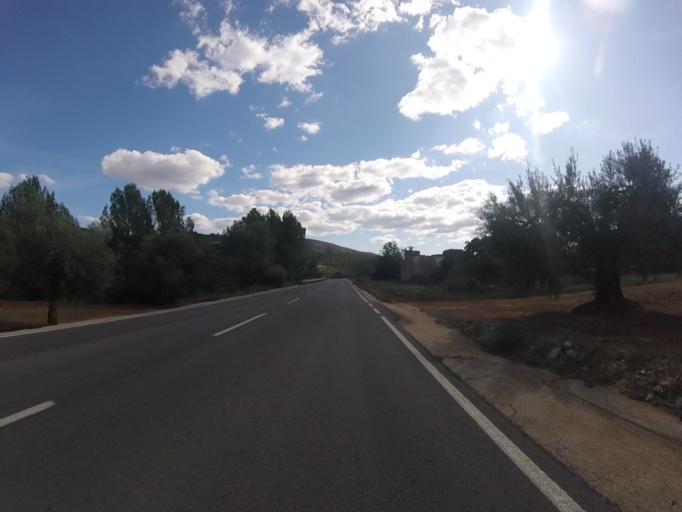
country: ES
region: Valencia
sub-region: Provincia de Castello
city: Cuevas de Vinroma
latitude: 40.3030
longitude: 0.1647
